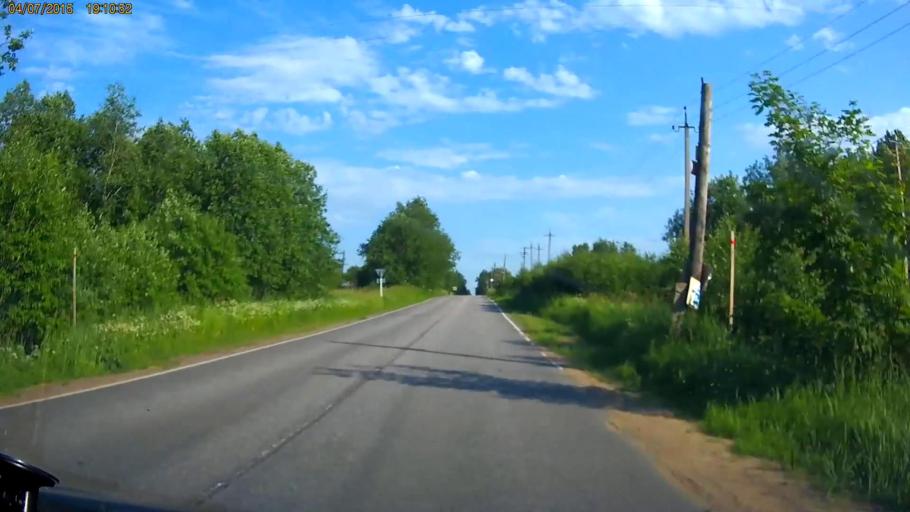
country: RU
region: Leningrad
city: Garbolovo
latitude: 60.3338
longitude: 30.4859
